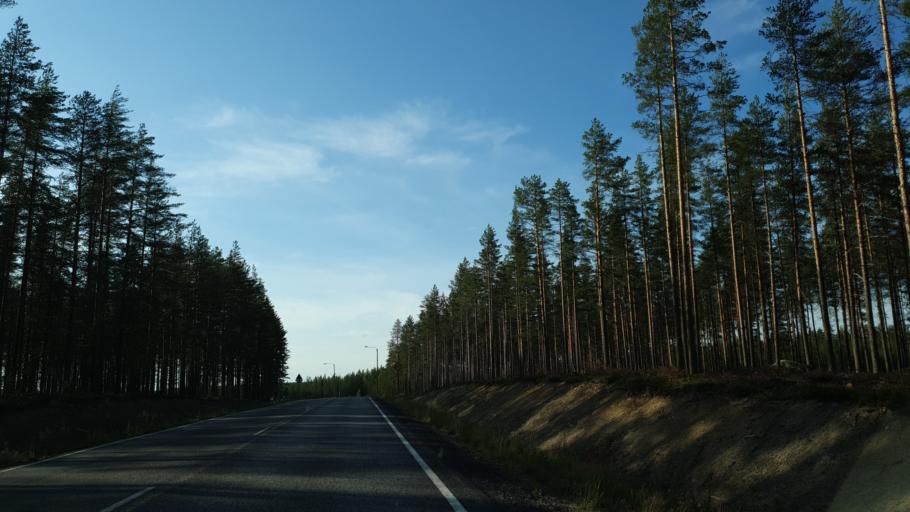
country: FI
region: Kainuu
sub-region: Kehys-Kainuu
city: Kuhmo
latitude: 64.0974
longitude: 29.4760
